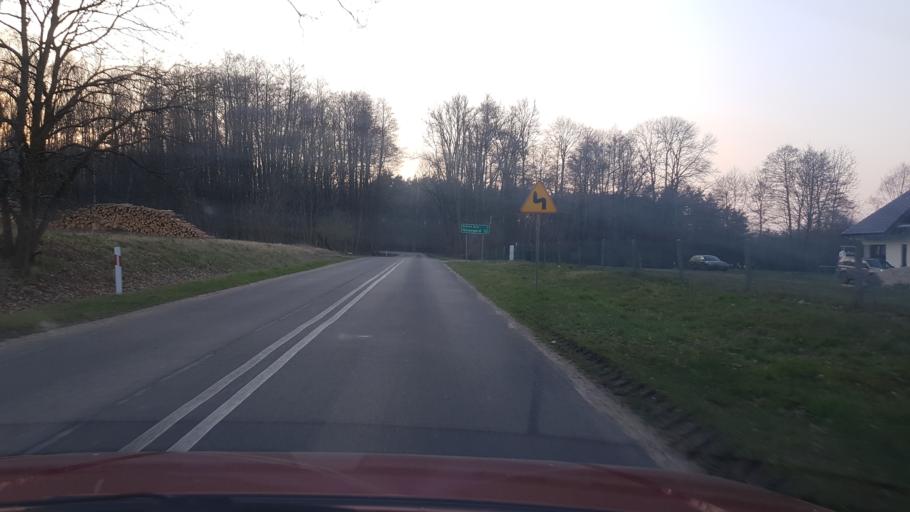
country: PL
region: West Pomeranian Voivodeship
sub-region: Powiat lobeski
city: Radowo Male
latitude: 53.6518
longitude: 15.5233
